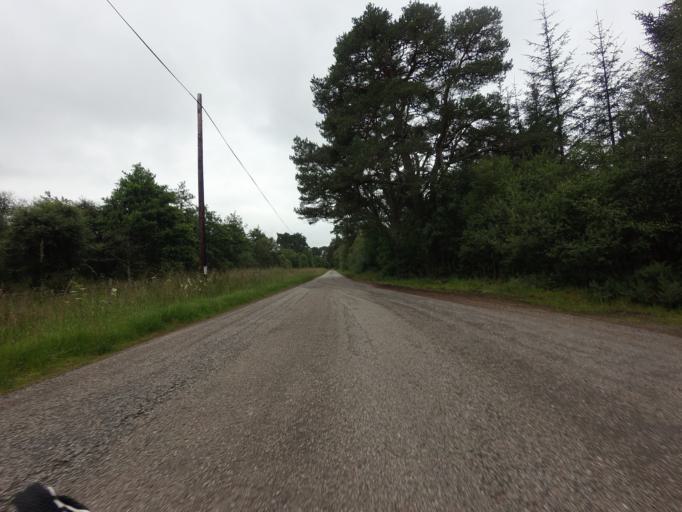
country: GB
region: Scotland
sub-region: Highland
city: Alness
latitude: 57.9906
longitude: -4.4112
